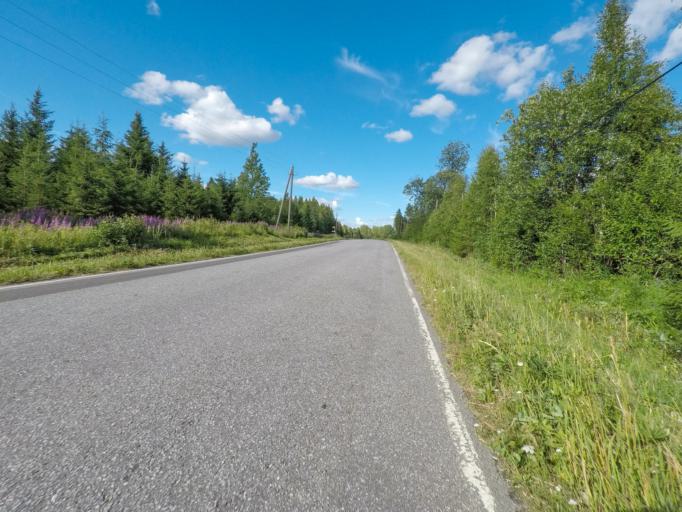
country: FI
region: South Karelia
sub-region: Imatra
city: Imatra
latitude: 61.1378
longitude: 28.7372
